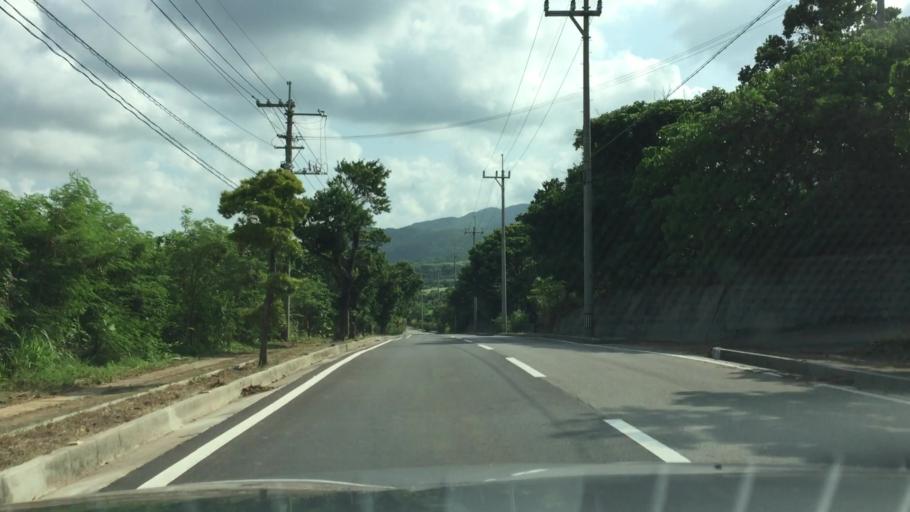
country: JP
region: Okinawa
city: Ishigaki
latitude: 24.4707
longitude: 124.2530
